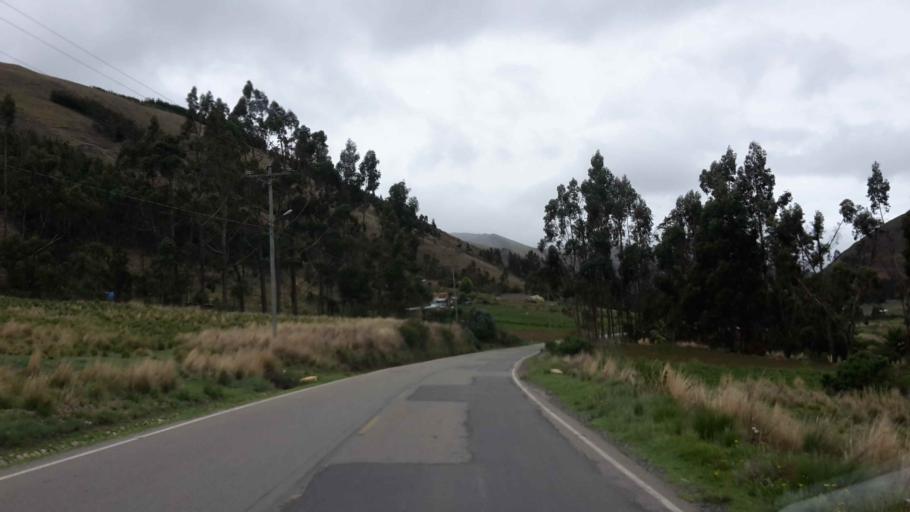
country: BO
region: Cochabamba
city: Arani
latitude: -17.4793
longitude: -65.5433
